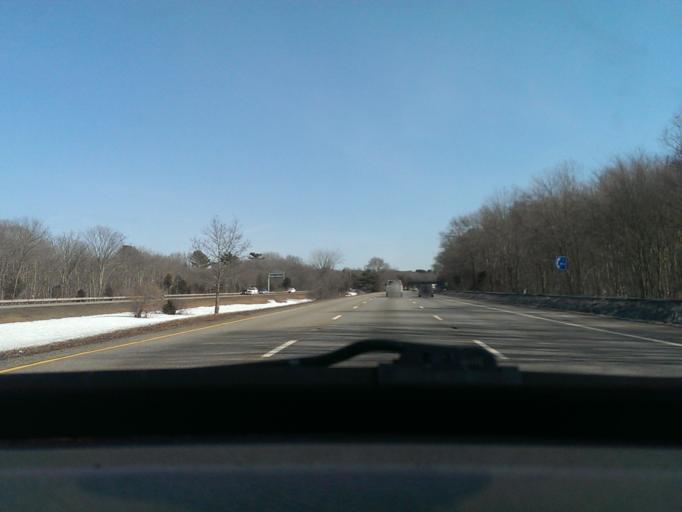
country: US
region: Rhode Island
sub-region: Bristol County
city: Warren
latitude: 41.7719
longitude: -71.2529
